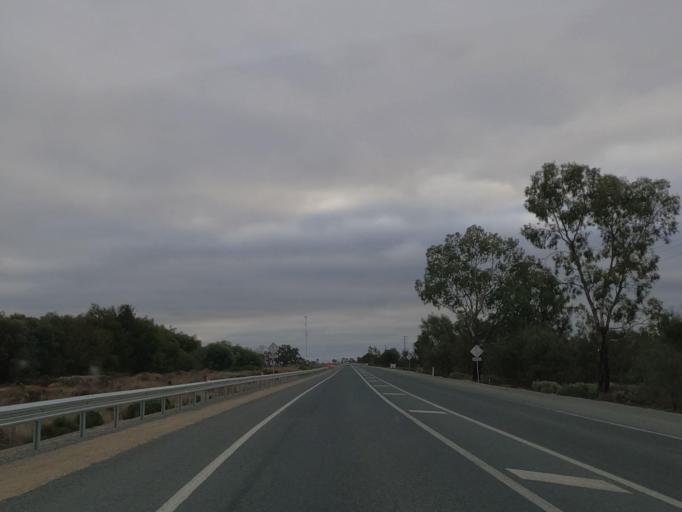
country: AU
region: Victoria
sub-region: Swan Hill
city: Swan Hill
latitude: -35.5354
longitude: 143.7449
